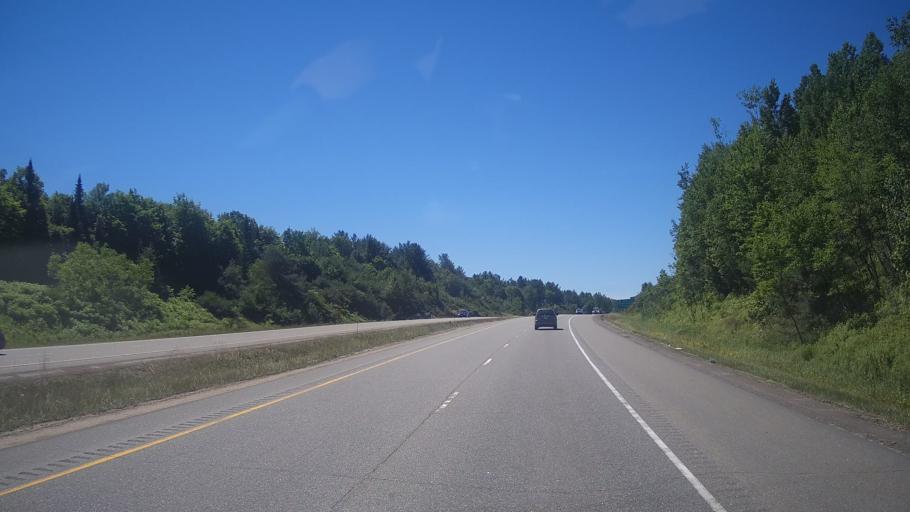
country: CA
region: Ontario
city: Bracebridge
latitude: 45.0271
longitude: -79.2923
